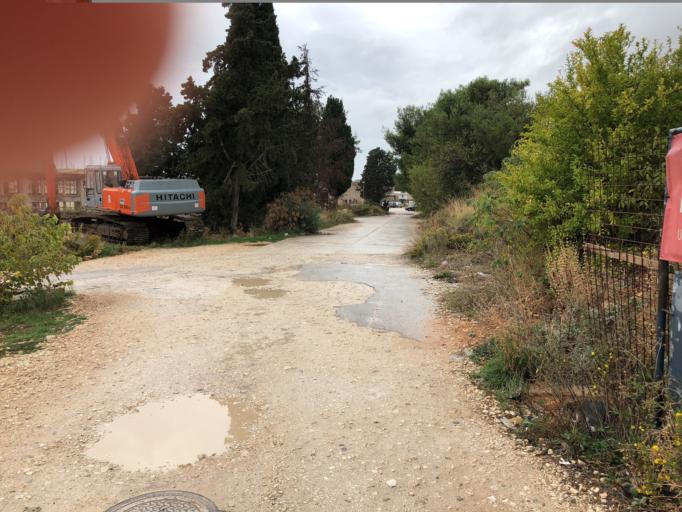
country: HR
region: Splitsko-Dalmatinska
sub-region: Grad Trogir
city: Trogir
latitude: 43.5171
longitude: 16.2361
